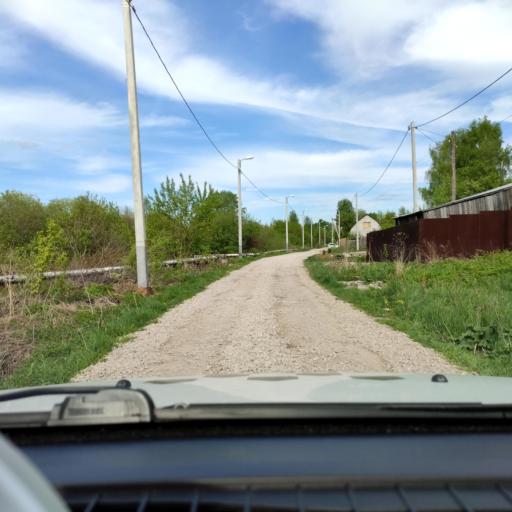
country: RU
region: Perm
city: Kondratovo
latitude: 58.0038
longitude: 56.1024
